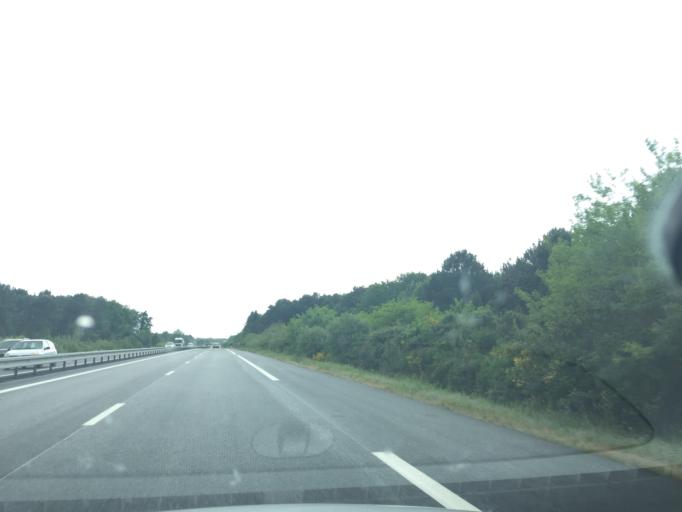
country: FR
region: Pays de la Loire
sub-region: Departement de la Sarthe
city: Brette-les-Pins
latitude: 47.9493
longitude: 0.3211
